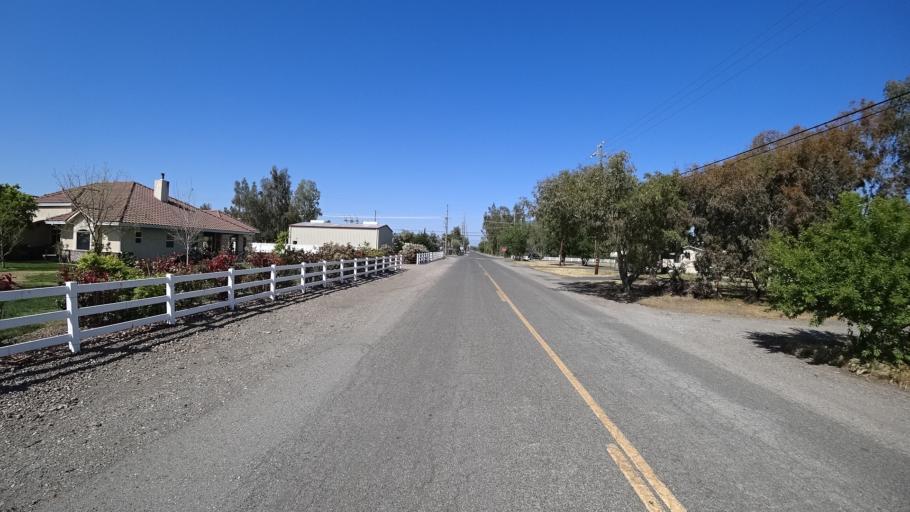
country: US
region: California
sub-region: Glenn County
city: Orland
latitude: 39.7255
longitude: -122.1772
